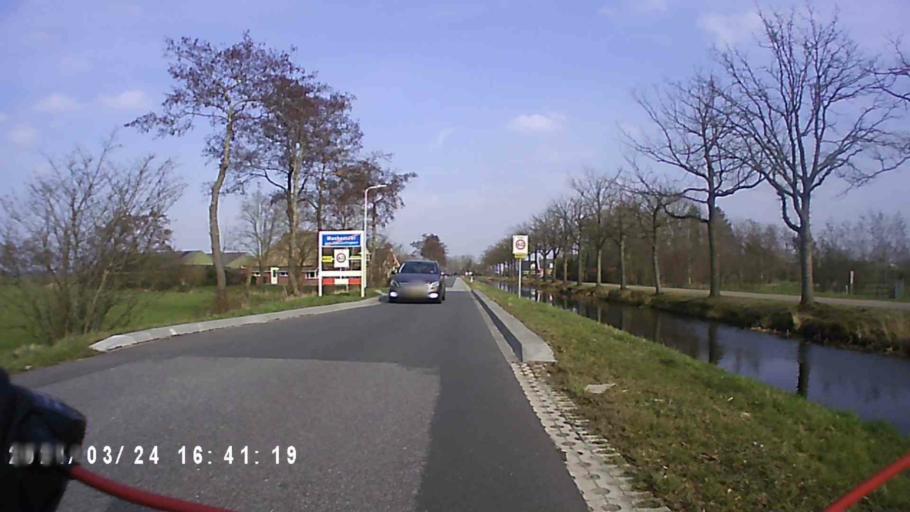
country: NL
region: Groningen
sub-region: Gemeente Leek
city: Leek
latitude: 53.0581
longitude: 6.2862
